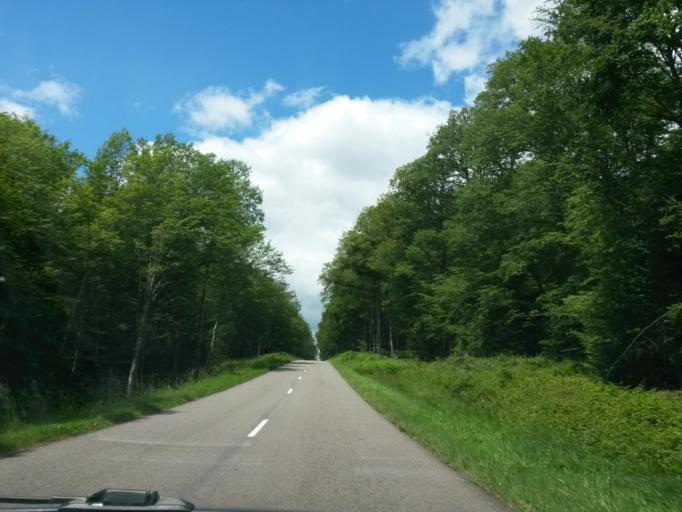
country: FR
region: Bourgogne
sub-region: Departement de la Nievre
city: Premery
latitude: 47.1829
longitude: 3.2819
